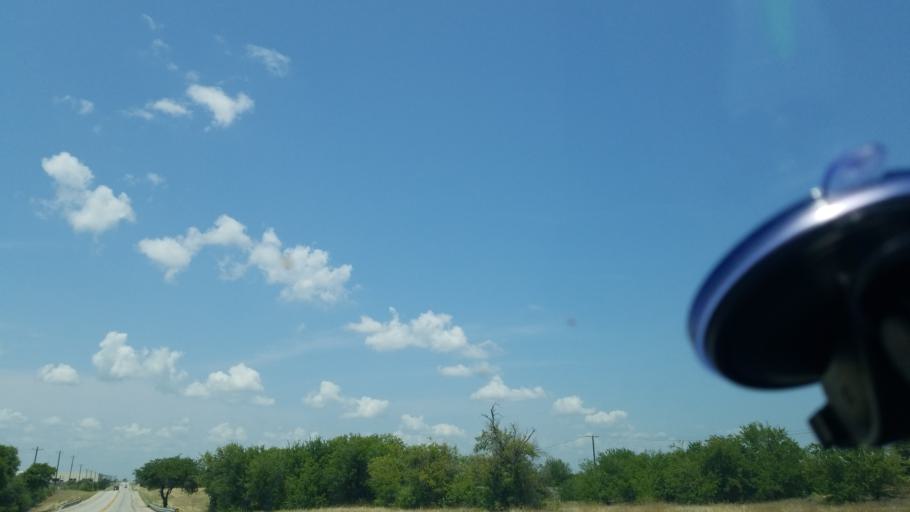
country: US
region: Texas
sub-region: Tarrant County
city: Eagle Mountain
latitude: 32.9260
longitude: -97.4128
